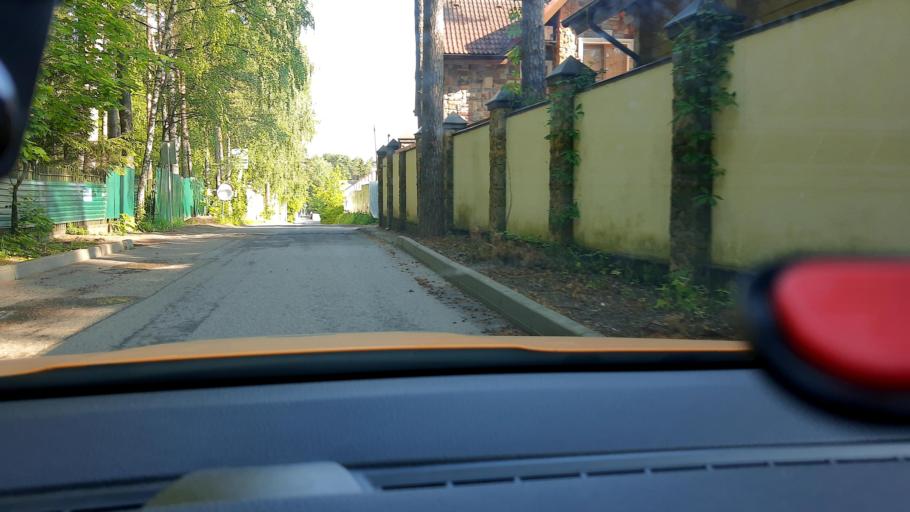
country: RU
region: Moskovskaya
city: Barvikha
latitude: 55.7315
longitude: 37.2480
